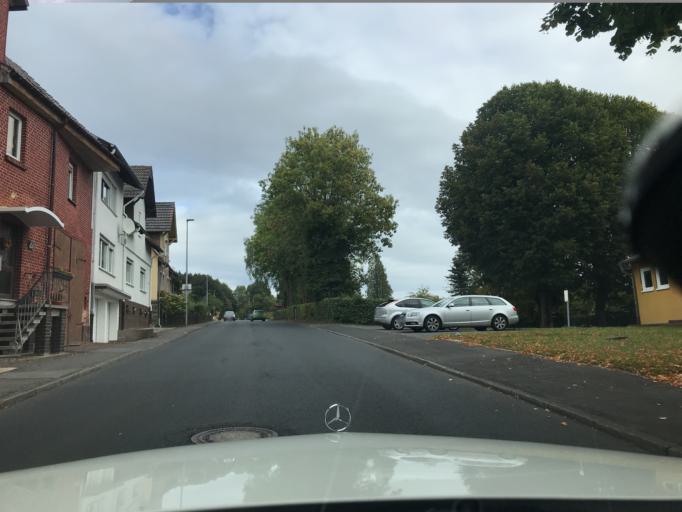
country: DE
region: Hesse
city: Hessisch Lichtenau
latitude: 51.2228
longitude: 9.7434
